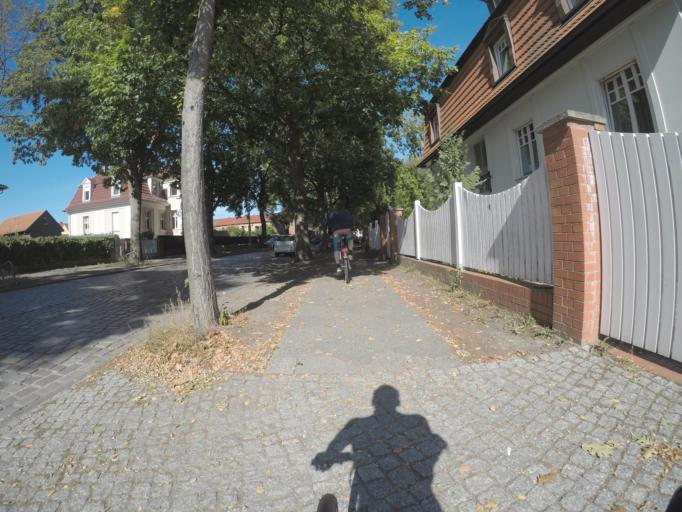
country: DE
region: Berlin
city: Konradshohe
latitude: 52.6040
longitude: 13.2097
